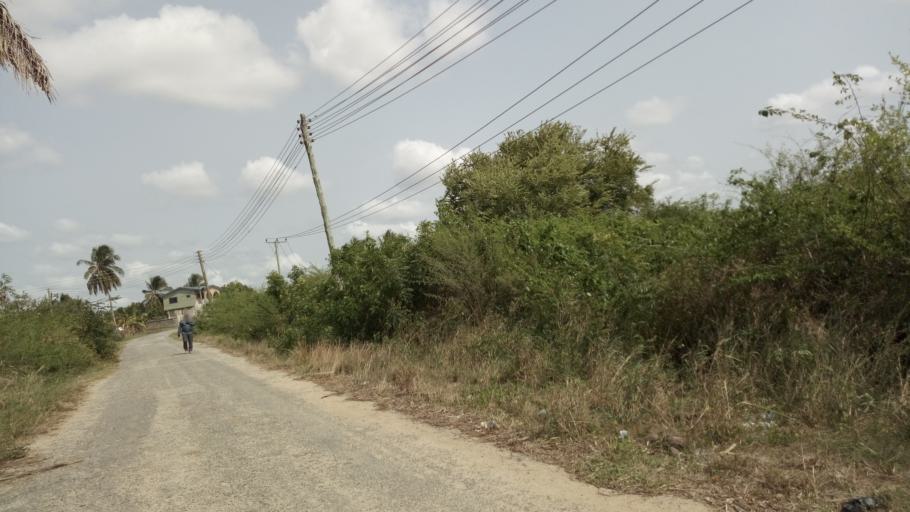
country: GH
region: Central
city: Winneba
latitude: 5.3677
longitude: -0.6430
